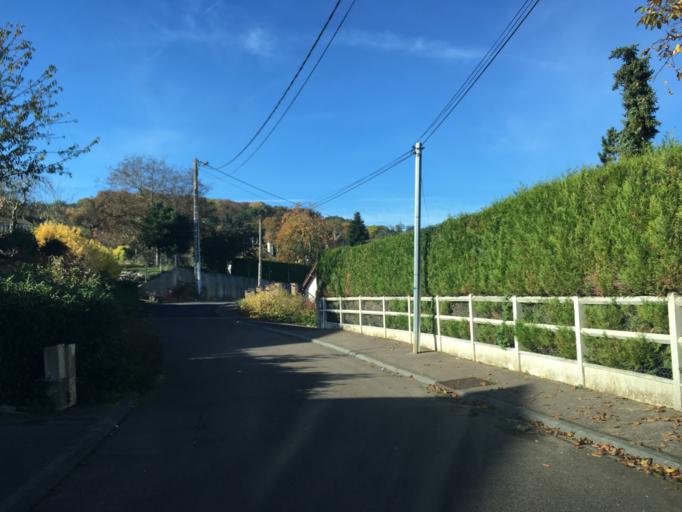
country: FR
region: Haute-Normandie
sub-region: Departement de l'Eure
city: Vernon
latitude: 49.0846
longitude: 1.4611
